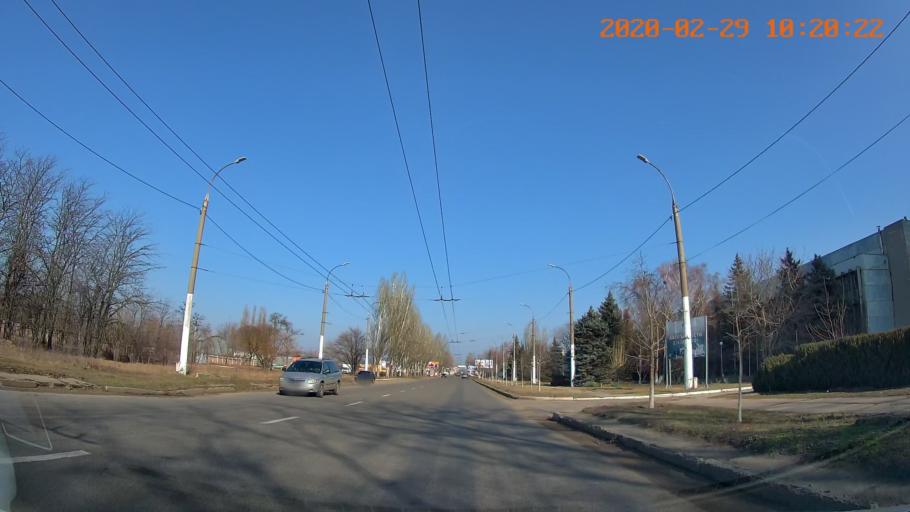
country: MD
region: Telenesti
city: Tiraspolul Nou
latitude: 46.8596
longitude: 29.6107
